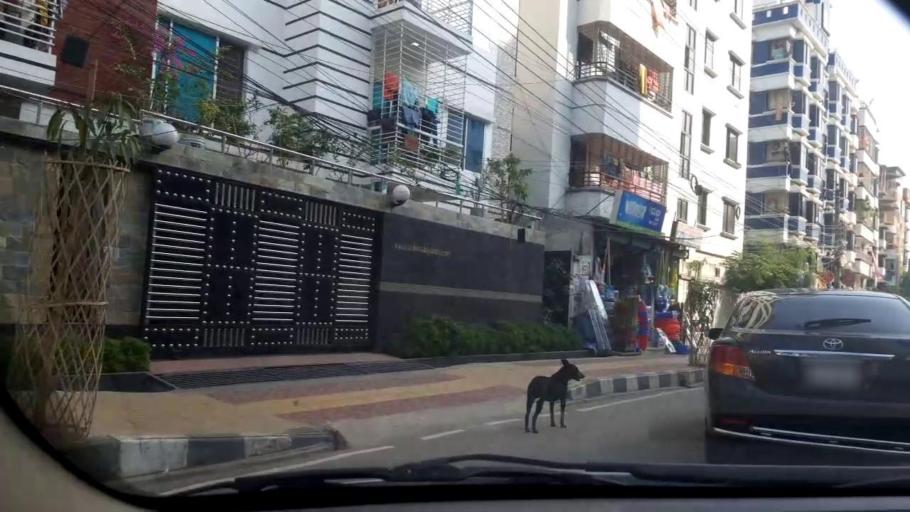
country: BD
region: Dhaka
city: Tungi
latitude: 23.8670
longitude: 90.3886
